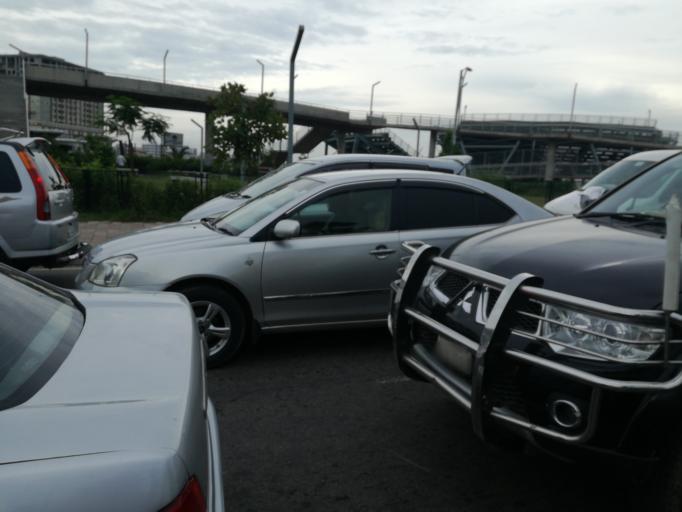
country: BD
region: Dhaka
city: Paltan
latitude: 23.7715
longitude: 90.4127
